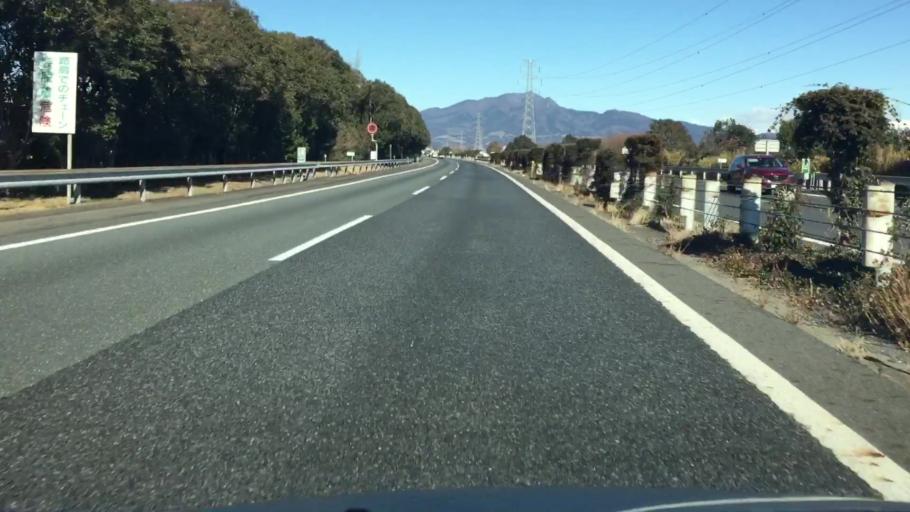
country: JP
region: Gunma
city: Shibukawa
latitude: 36.4517
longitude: 139.0146
